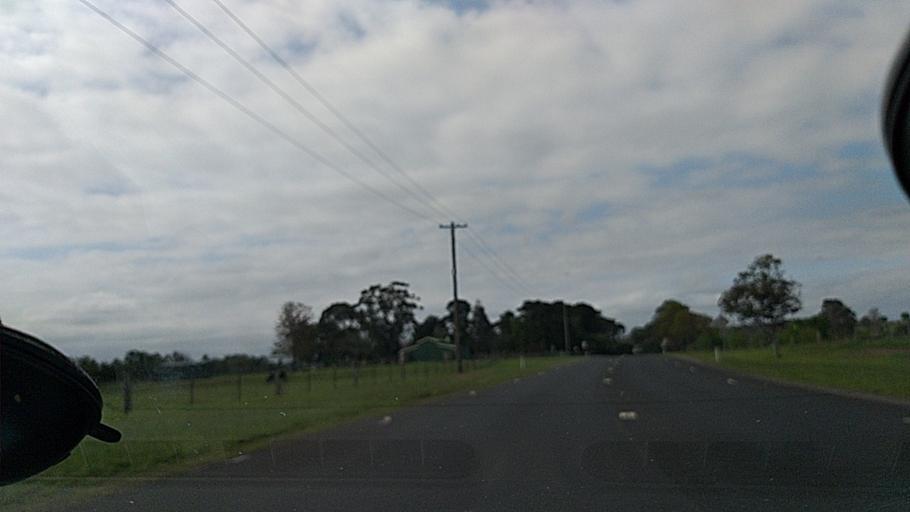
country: AU
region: New South Wales
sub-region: Campbelltown Municipality
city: Glen Alpine
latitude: -34.1135
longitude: 150.7435
